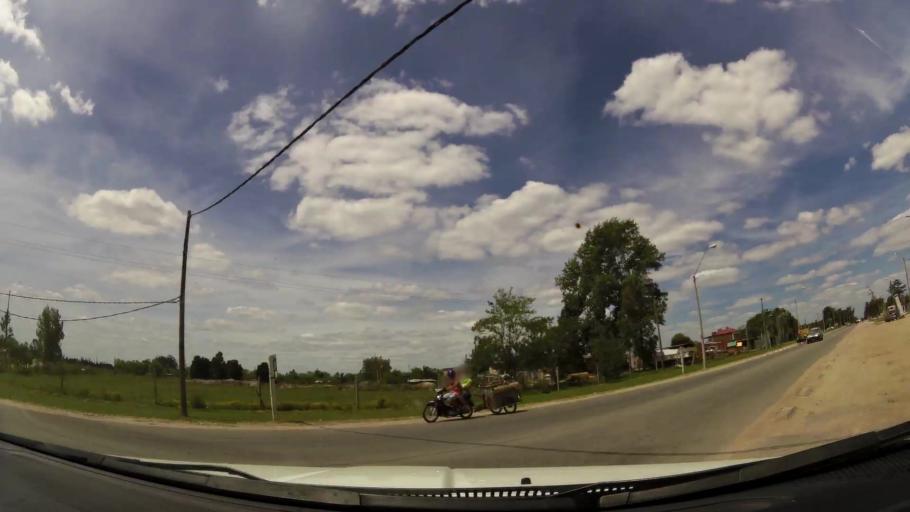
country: UY
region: San Jose
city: Delta del Tigre
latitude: -34.7395
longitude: -56.4389
